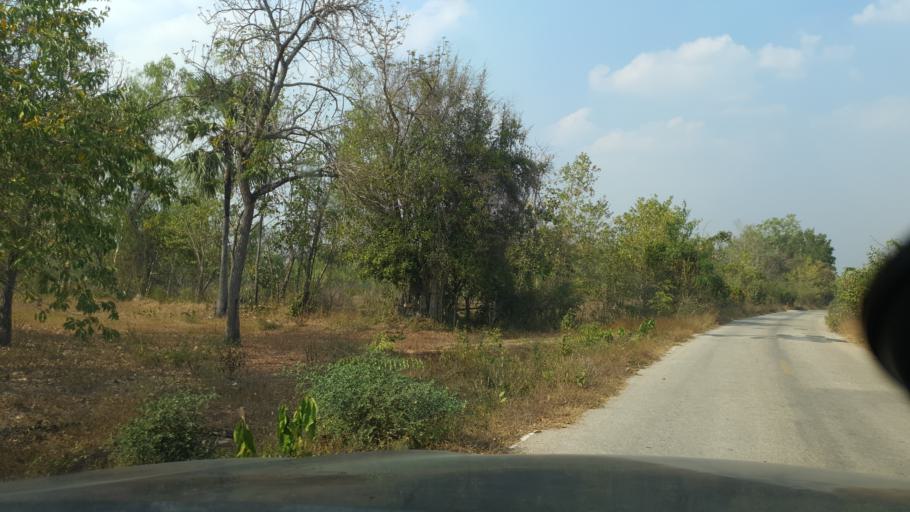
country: TH
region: Sukhothai
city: Ban Dan Lan Hoi
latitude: 17.0153
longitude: 99.5582
